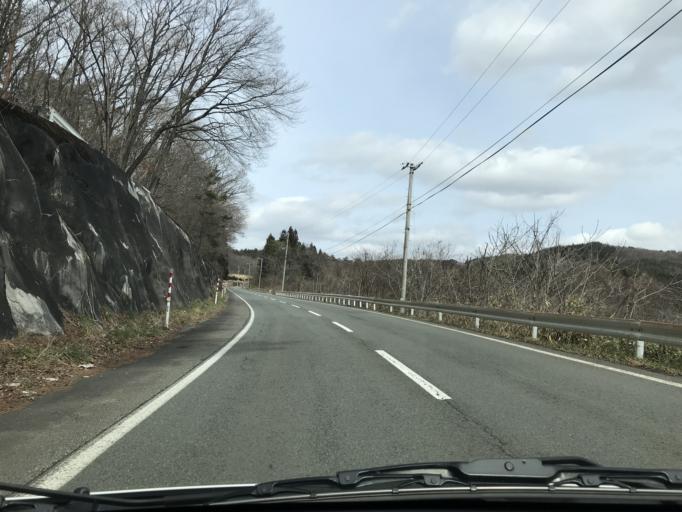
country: JP
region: Iwate
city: Tono
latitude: 39.3060
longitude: 141.3699
